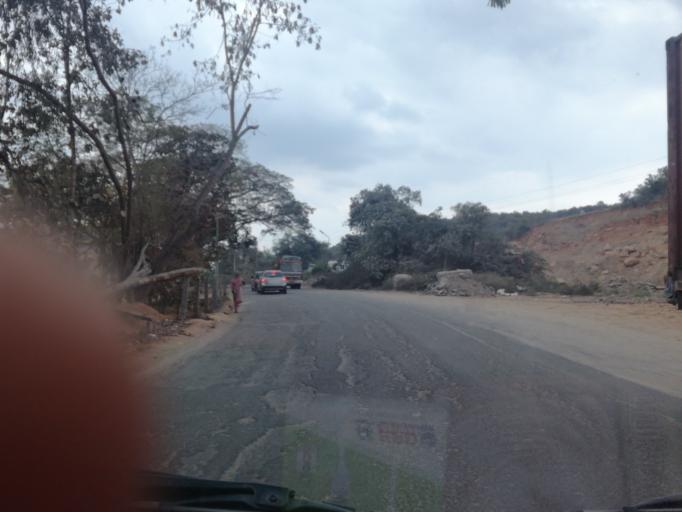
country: IN
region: Andhra Pradesh
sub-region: Chittoor
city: Ramapuram
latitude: 13.0898
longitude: 79.1341
